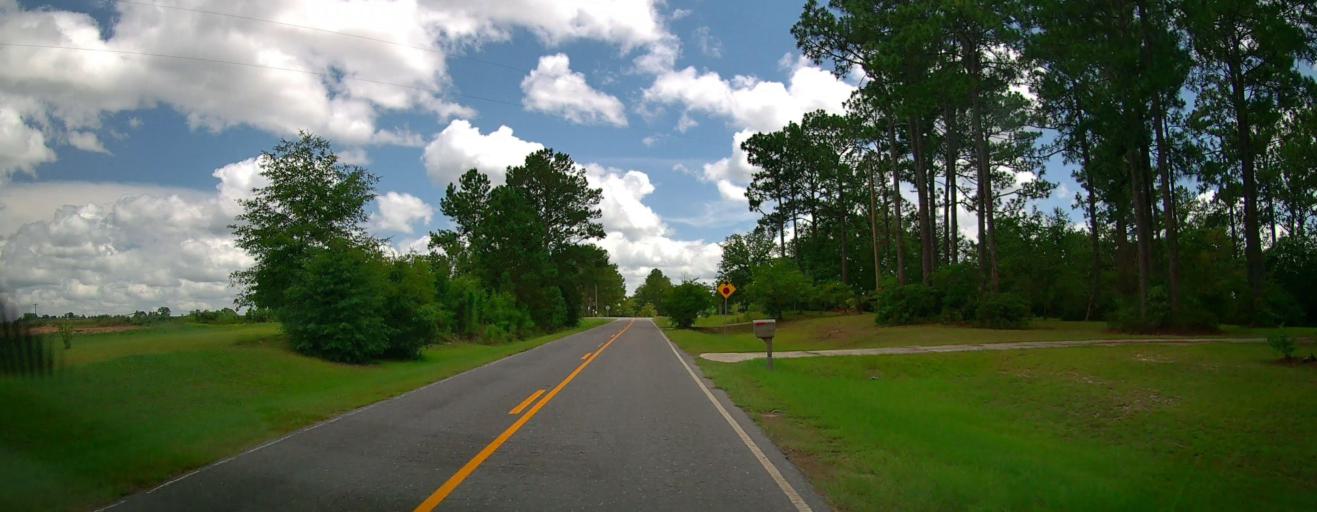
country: US
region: Georgia
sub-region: Irwin County
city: Ocilla
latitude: 31.6454
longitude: -83.3961
